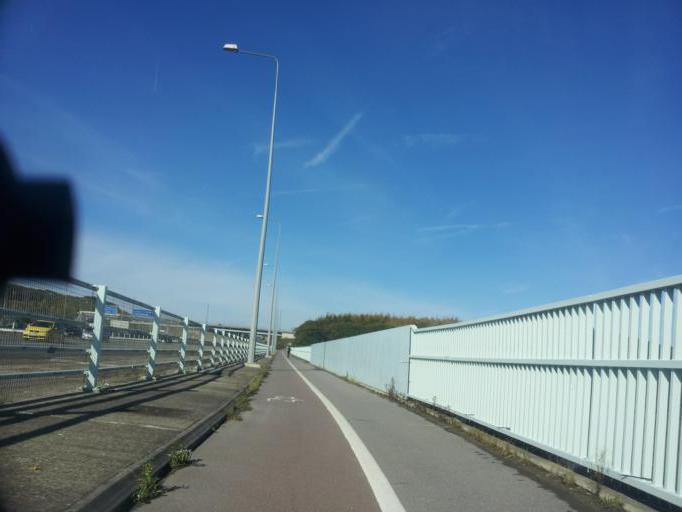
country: GB
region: England
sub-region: Medway
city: Cuxton
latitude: 51.3792
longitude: 0.4732
